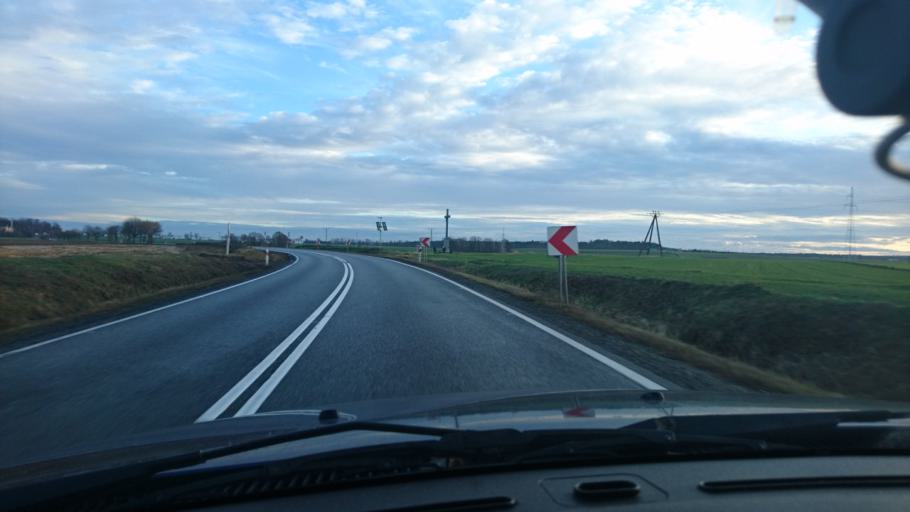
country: PL
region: Greater Poland Voivodeship
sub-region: Powiat kepinski
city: Baranow
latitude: 51.2465
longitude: 18.0183
